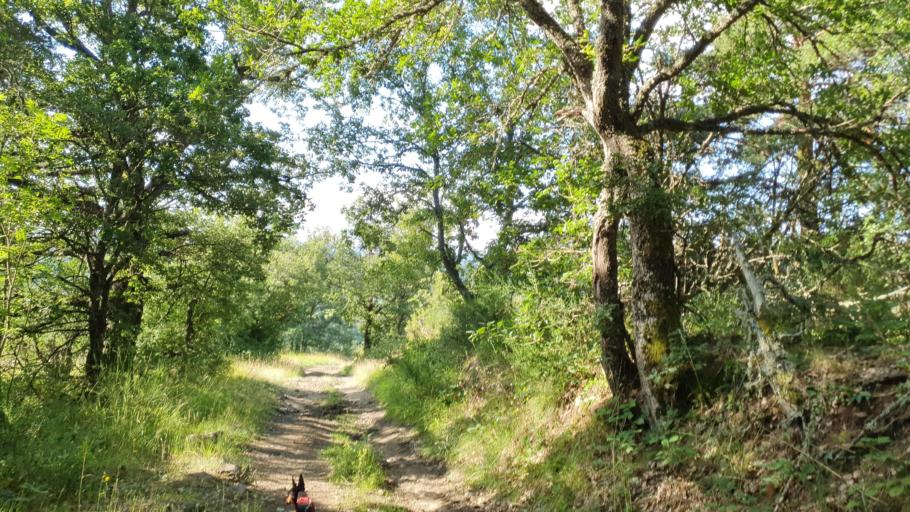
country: FR
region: Auvergne
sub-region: Departement du Puy-de-Dome
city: Aydat
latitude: 45.5801
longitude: 3.0179
